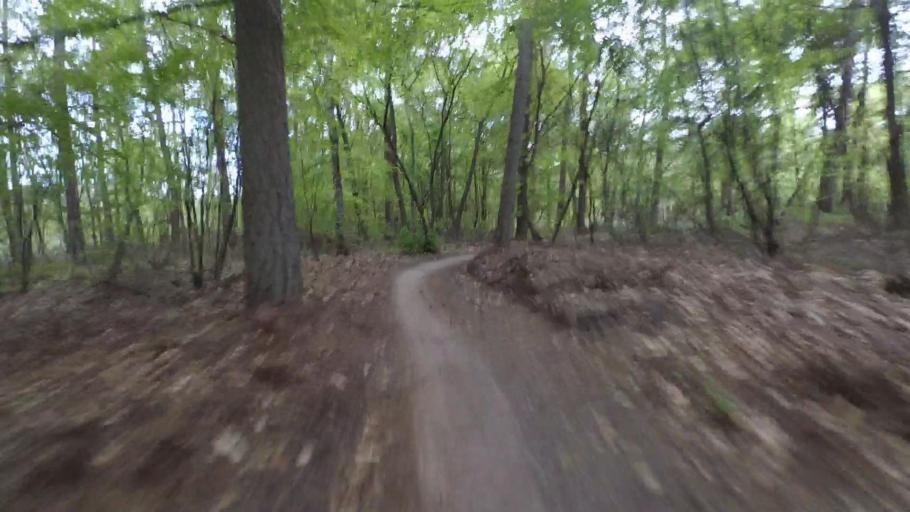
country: NL
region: Utrecht
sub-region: Gemeente Utrechtse Heuvelrug
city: Maarn
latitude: 52.0829
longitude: 5.3276
